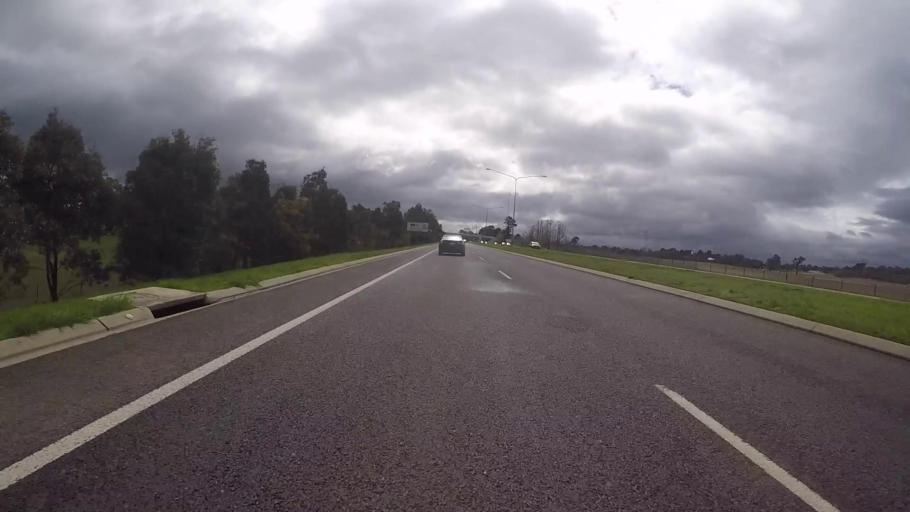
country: AU
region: Australian Capital Territory
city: Kaleen
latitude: -35.2297
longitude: 149.1240
